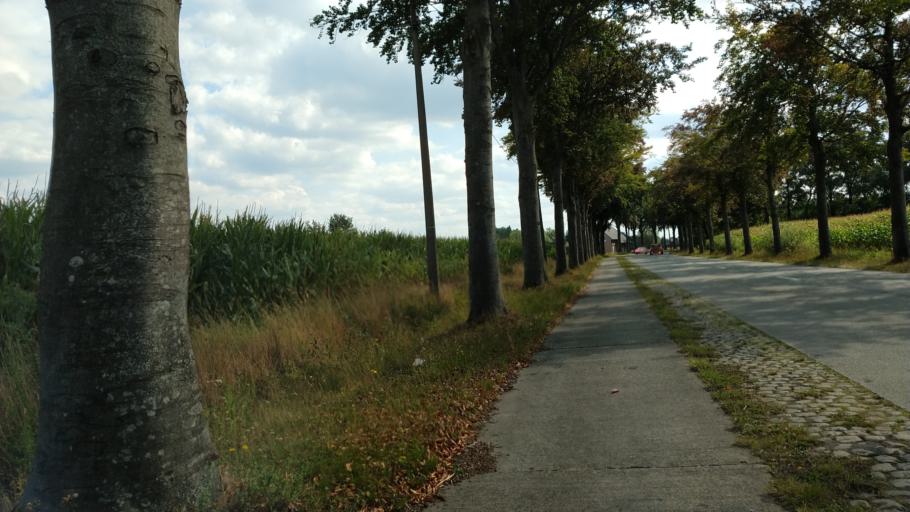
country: BE
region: Flanders
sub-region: Provincie Oost-Vlaanderen
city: Assenede
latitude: 51.2036
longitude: 3.6857
